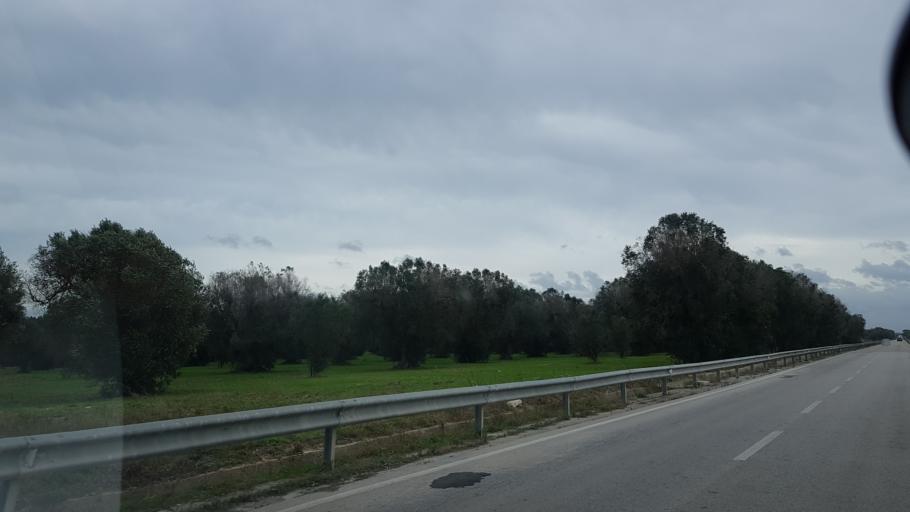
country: IT
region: Apulia
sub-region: Provincia di Brindisi
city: San Pancrazio Salentino
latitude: 40.4083
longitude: 17.8806
